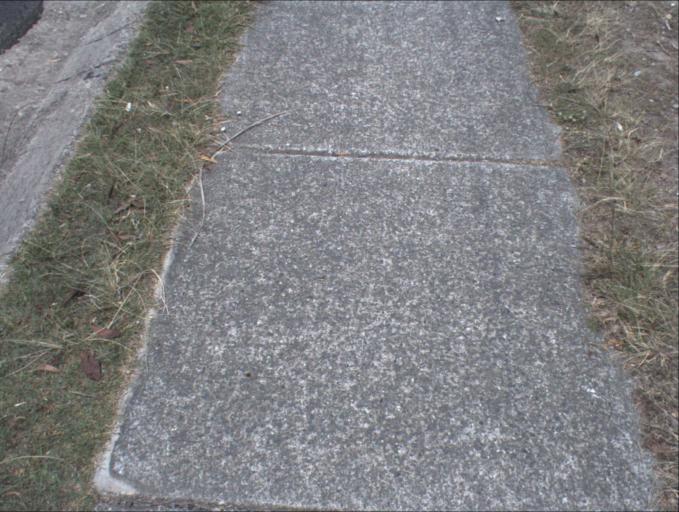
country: AU
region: Queensland
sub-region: Logan
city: Beenleigh
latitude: -27.6956
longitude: 153.2167
